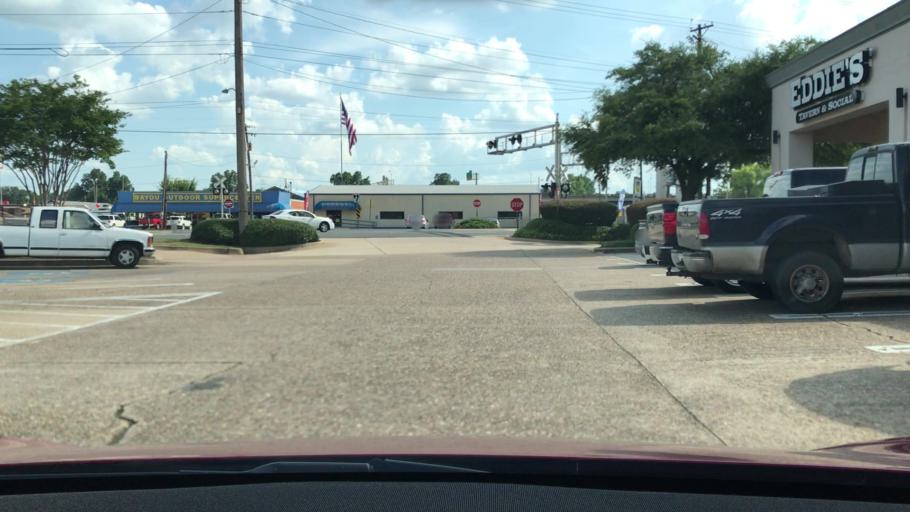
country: US
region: Louisiana
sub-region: Bossier Parish
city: Bossier City
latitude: 32.5164
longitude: -93.7190
